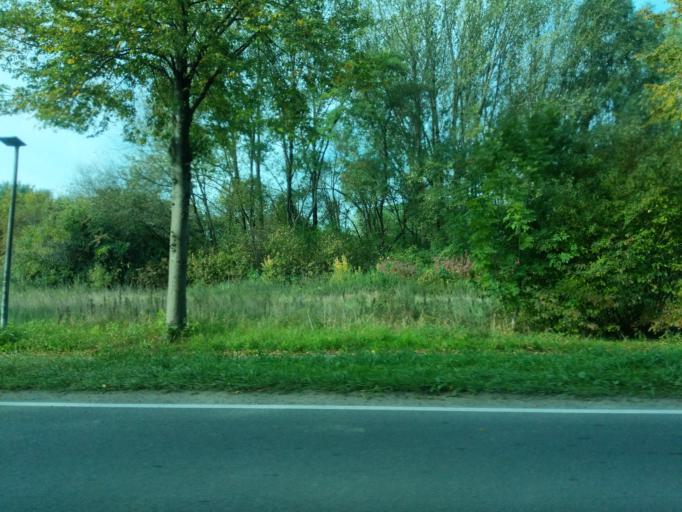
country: DE
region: Schleswig-Holstein
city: Lagerdorf
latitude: 53.8734
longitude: 9.5893
